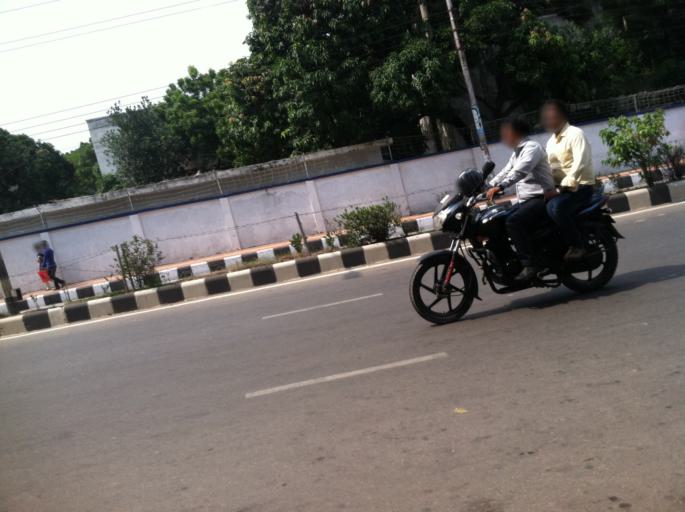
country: BD
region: Dhaka
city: Paltan
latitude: 23.7931
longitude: 90.4150
